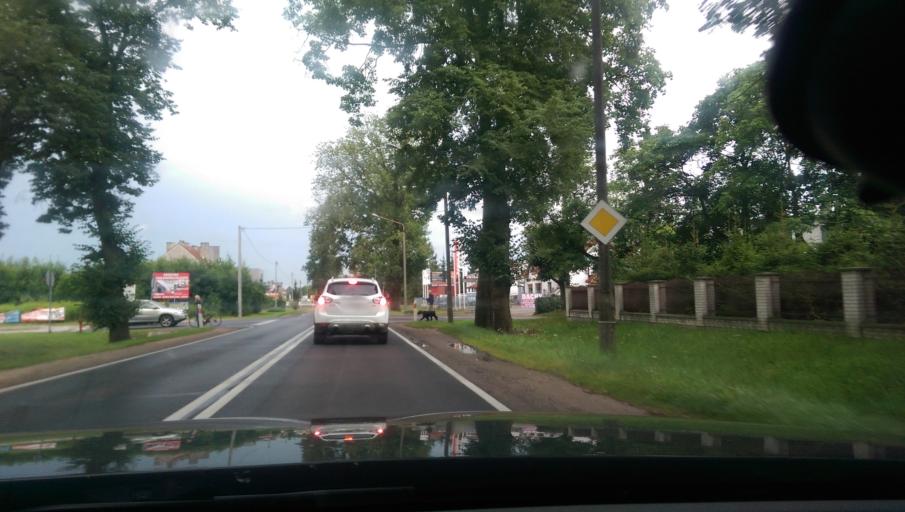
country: PL
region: Warmian-Masurian Voivodeship
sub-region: Powiat szczycienski
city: Szczytno
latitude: 53.5551
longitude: 20.9875
